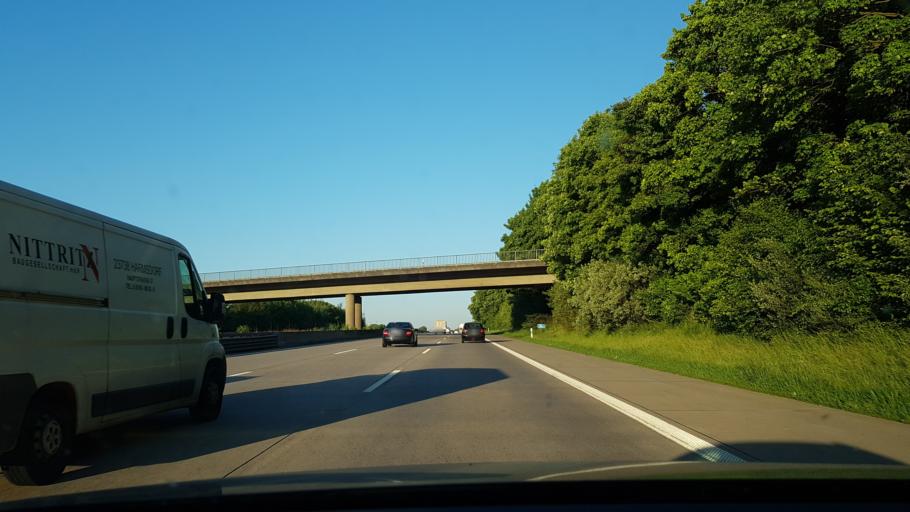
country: DE
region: Schleswig-Holstein
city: Politz
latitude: 53.7695
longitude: 10.3942
